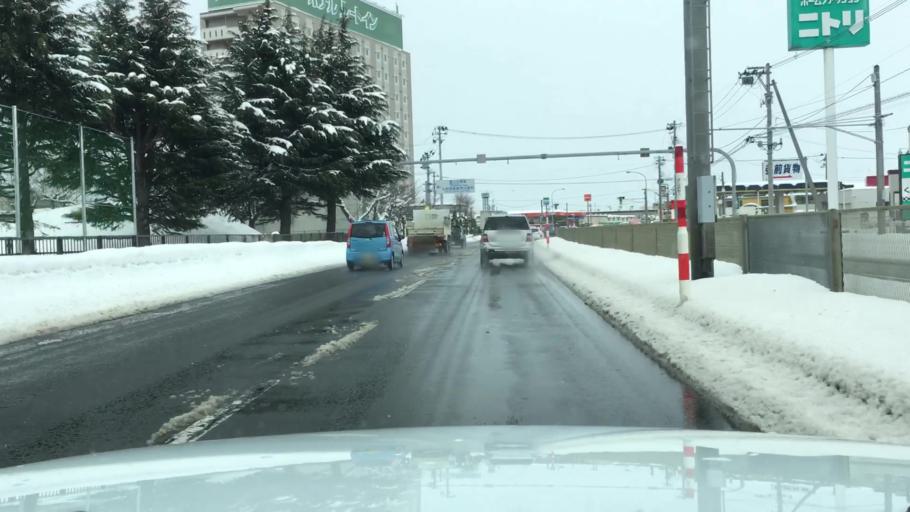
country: JP
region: Aomori
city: Hirosaki
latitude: 40.6023
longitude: 140.4998
